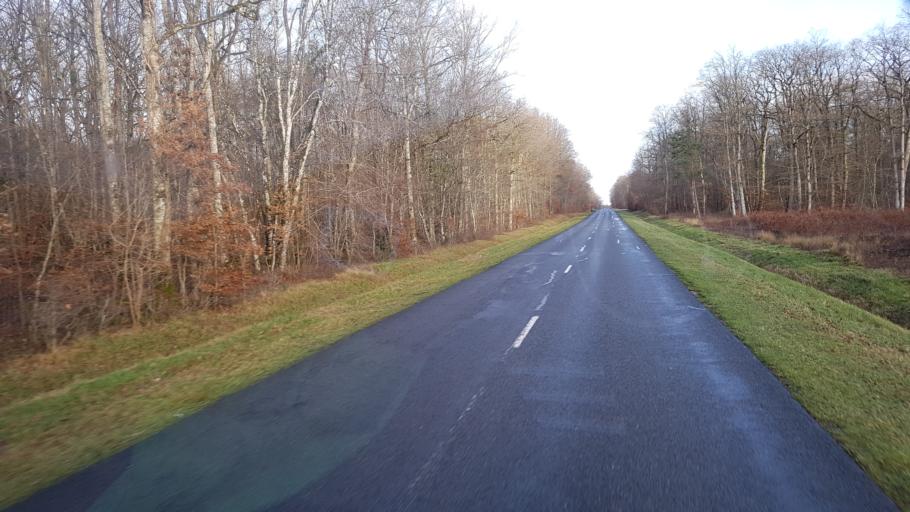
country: FR
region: Centre
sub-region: Departement du Loiret
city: Chilleurs-aux-Bois
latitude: 48.0283
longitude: 2.2104
